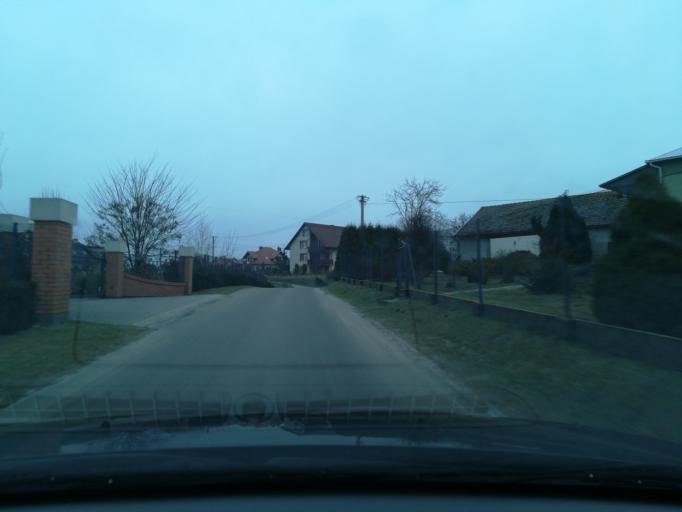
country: PL
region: Subcarpathian Voivodeship
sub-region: Powiat lancucki
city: Kosina
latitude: 50.0752
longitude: 22.3350
